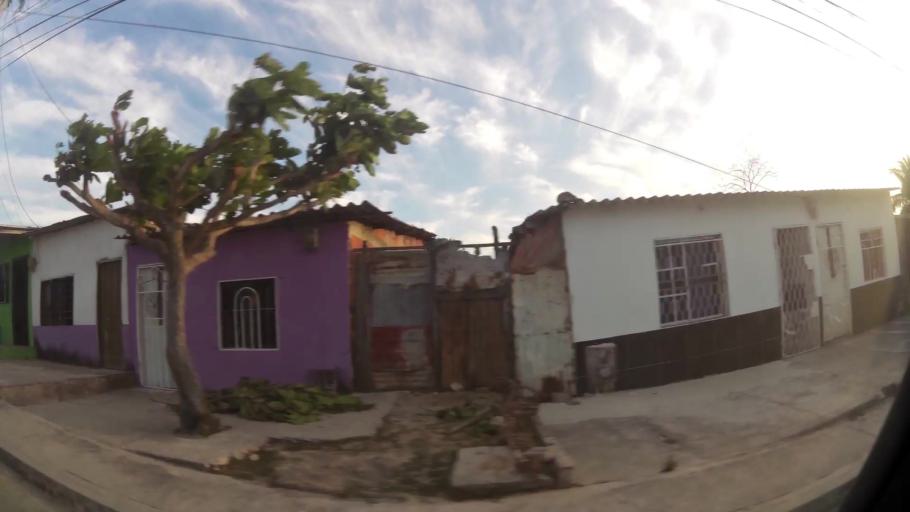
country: CO
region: Atlantico
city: Barranquilla
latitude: 10.9564
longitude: -74.8266
